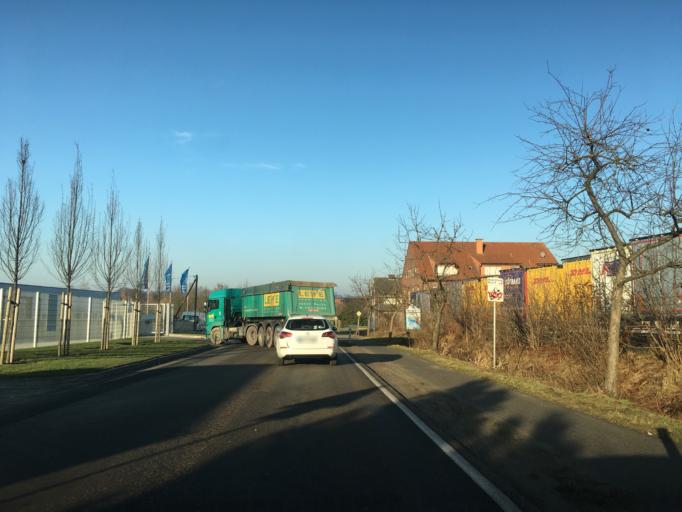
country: DE
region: North Rhine-Westphalia
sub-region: Regierungsbezirk Munster
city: Nordwalde
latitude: 52.0774
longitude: 7.4787
